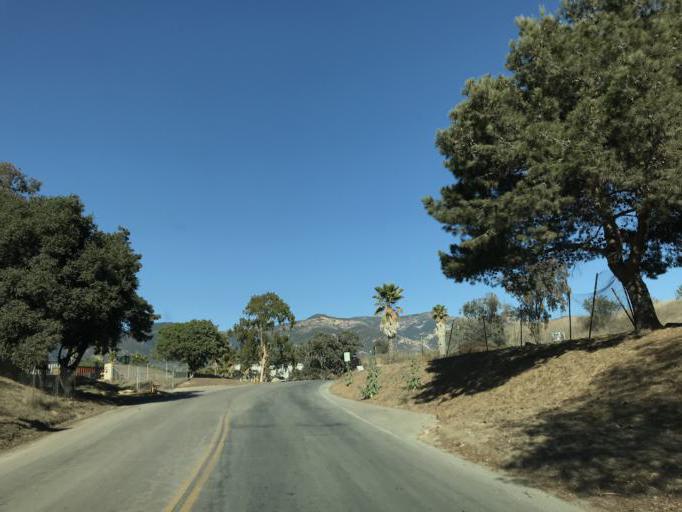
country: US
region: California
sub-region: Santa Barbara County
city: Goleta
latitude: 34.4465
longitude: -119.7743
